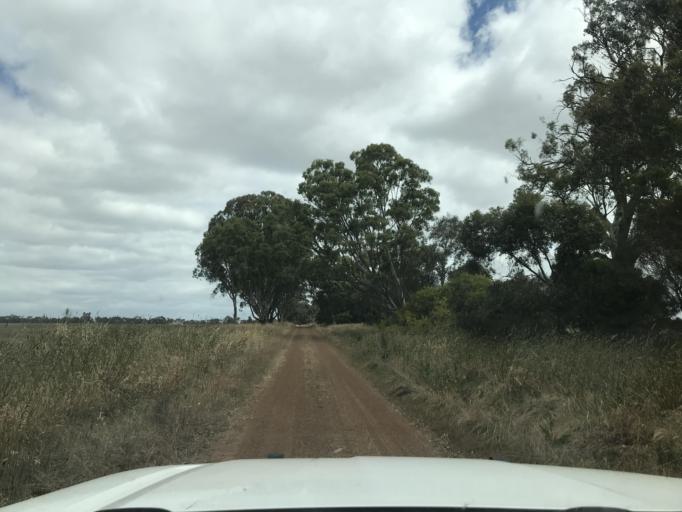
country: AU
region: South Australia
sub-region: Naracoorte and Lucindale
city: Naracoorte
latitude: -36.9837
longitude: 141.3906
